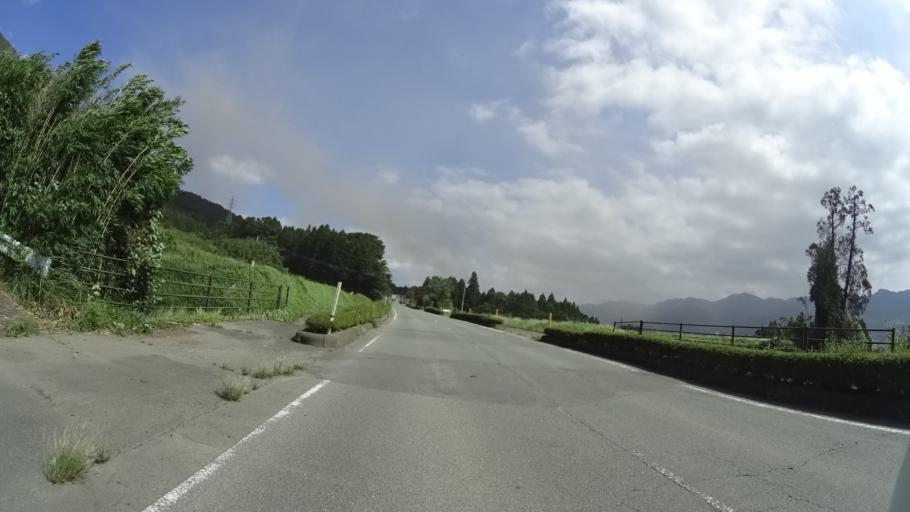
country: JP
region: Kumamoto
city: Aso
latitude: 32.8469
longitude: 131.0320
